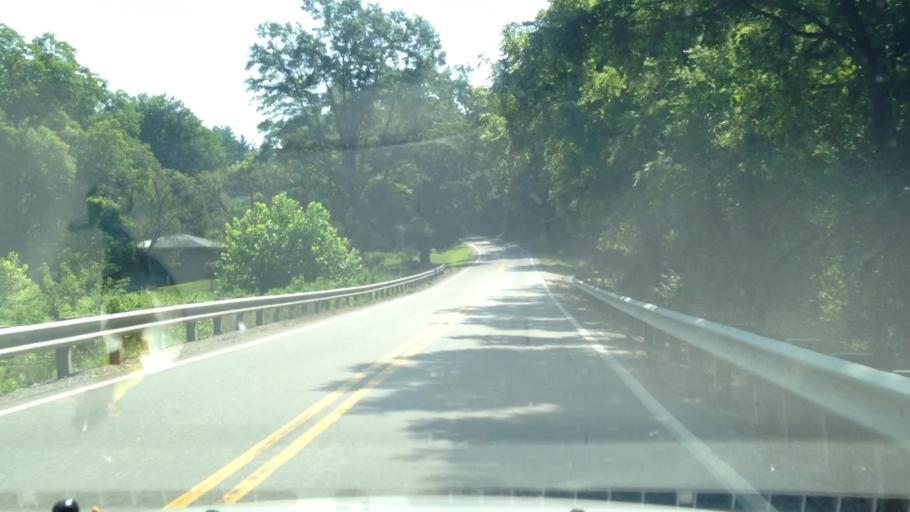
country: US
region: Virginia
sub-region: Patrick County
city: Stuart
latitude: 36.5768
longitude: -80.3773
